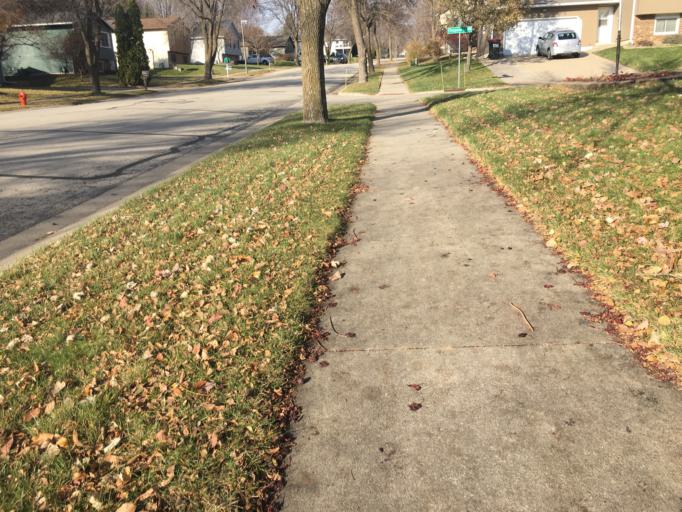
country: US
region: Minnesota
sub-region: Olmsted County
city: Rochester
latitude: 44.0798
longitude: -92.5219
